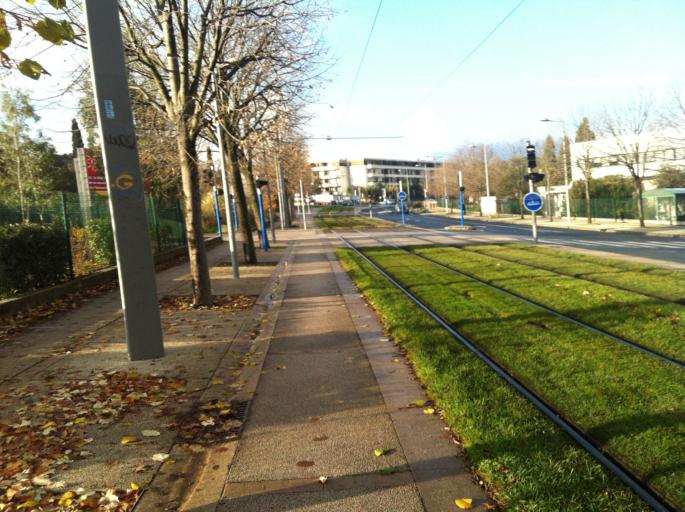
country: FR
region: Languedoc-Roussillon
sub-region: Departement de l'Herault
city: Montferrier-sur-Lez
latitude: 43.6354
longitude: 3.8458
